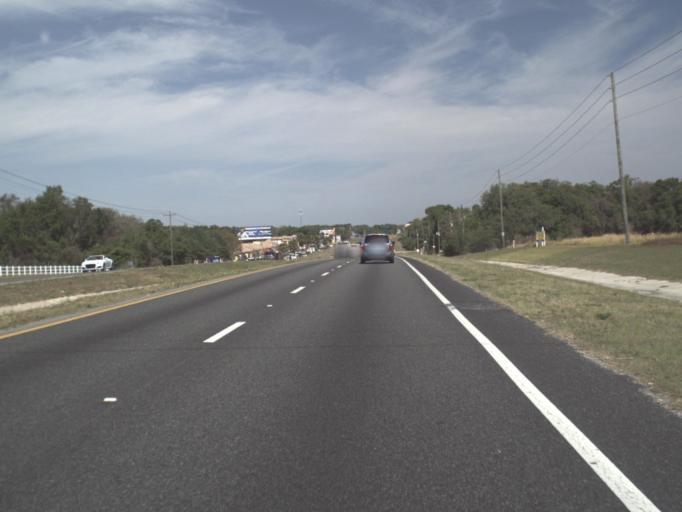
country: US
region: Florida
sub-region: Sumter County
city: The Villages
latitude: 28.9725
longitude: -81.9777
